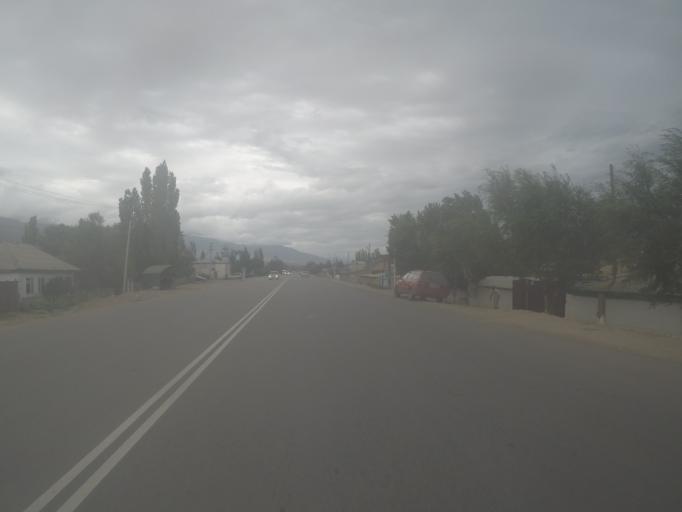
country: KG
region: Ysyk-Koel
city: Cholpon-Ata
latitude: 42.5863
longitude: 76.7426
